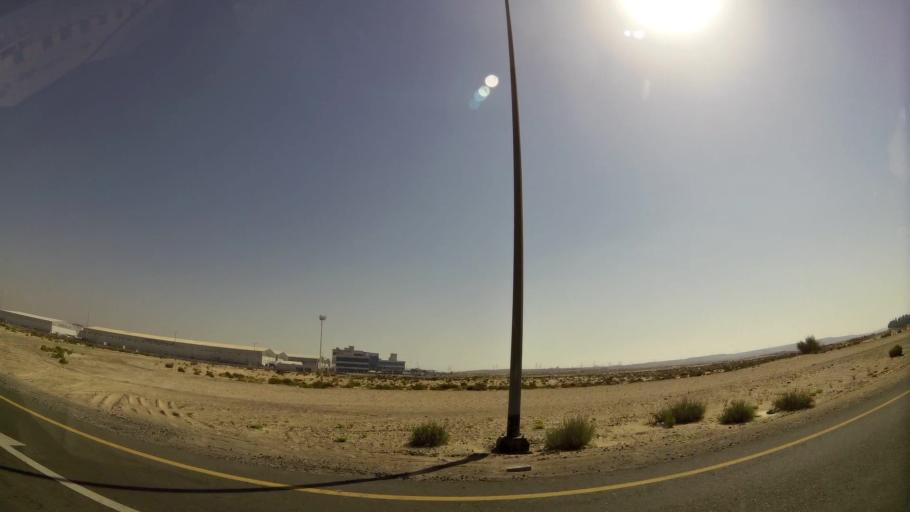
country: AE
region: Dubai
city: Dubai
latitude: 24.9241
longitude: 55.0587
